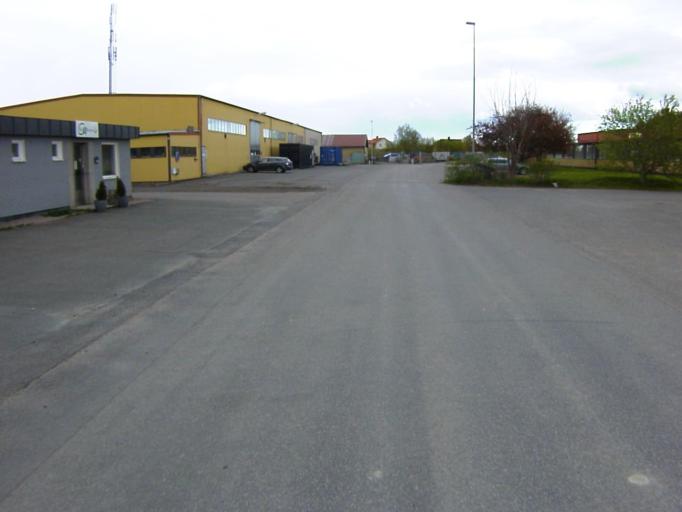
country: SE
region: Skane
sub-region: Kristianstads Kommun
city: Kristianstad
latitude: 56.0549
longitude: 14.1678
